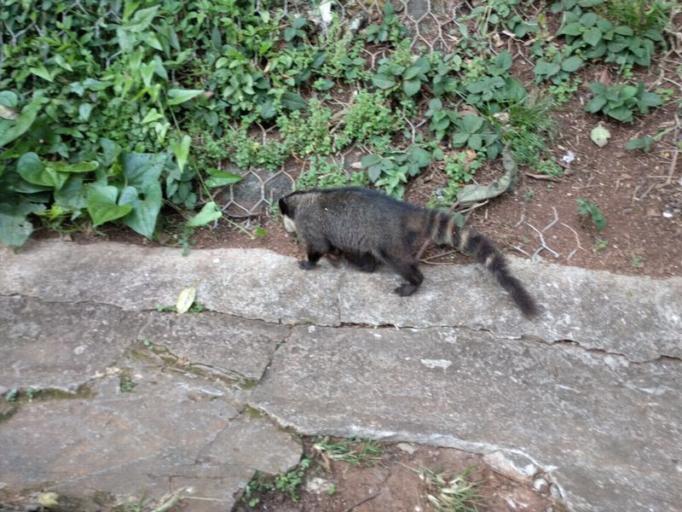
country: AR
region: Misiones
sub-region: Departamento de Iguazu
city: Puerto Iguazu
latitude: -25.6852
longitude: -54.4396
